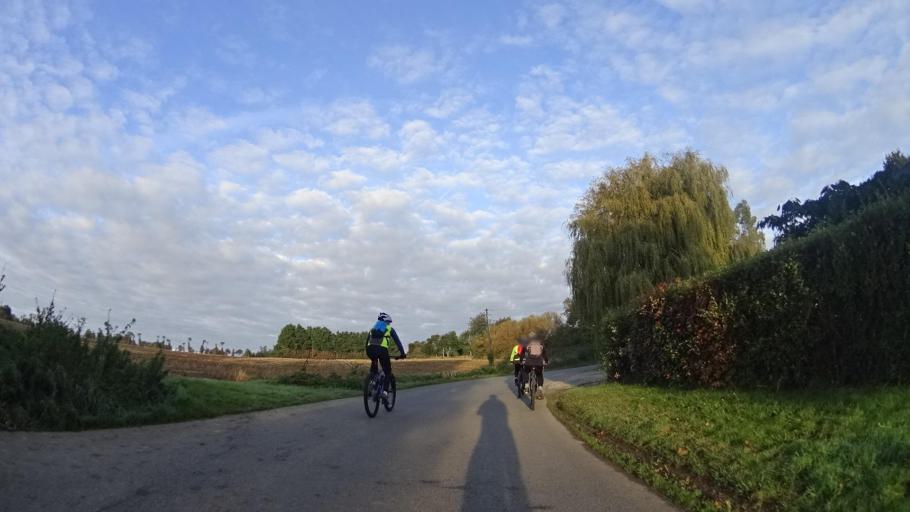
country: FR
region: Brittany
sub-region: Departement des Cotes-d'Armor
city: Evran
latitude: 48.3701
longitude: -1.9615
